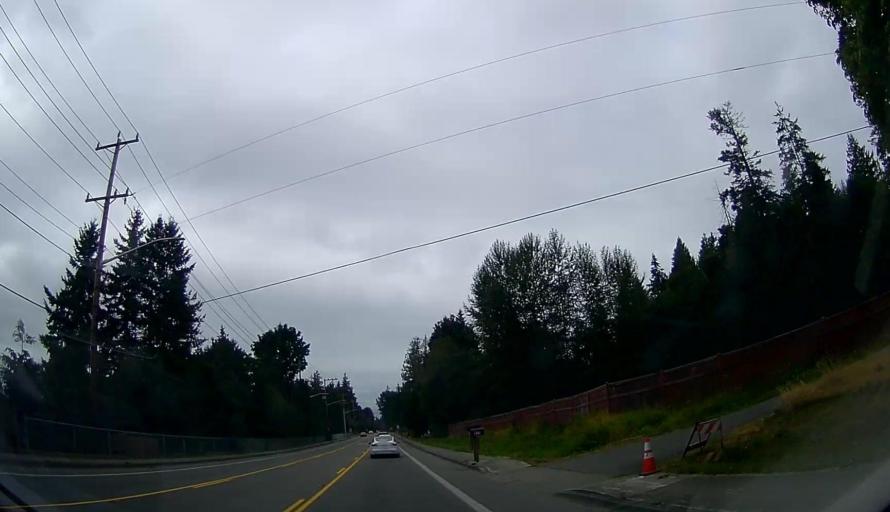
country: US
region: Washington
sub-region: Snohomish County
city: Marysville
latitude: 48.0440
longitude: -122.2194
